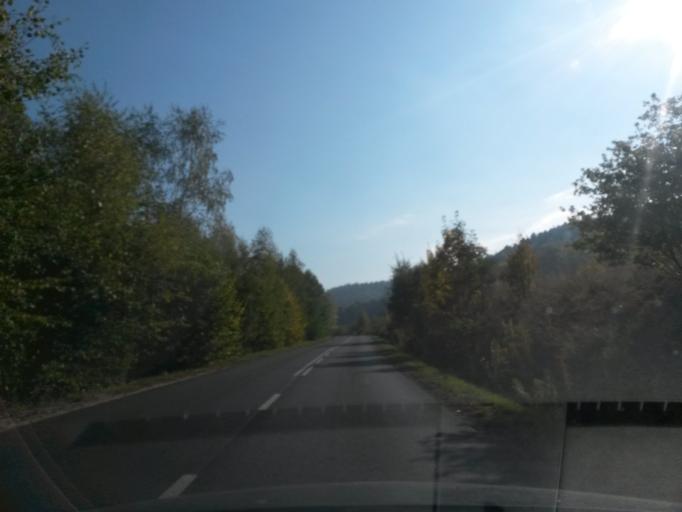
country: PL
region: Lower Silesian Voivodeship
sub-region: Powiat jeleniogorski
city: Piechowice
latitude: 50.8456
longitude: 15.6135
